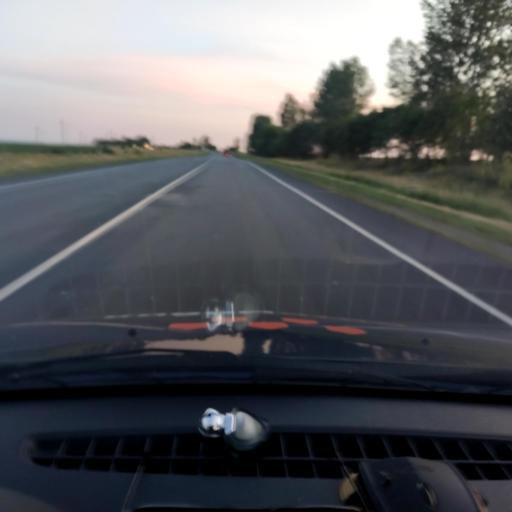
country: RU
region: Kursk
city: Gorshechnoye
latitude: 51.4970
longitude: 37.9781
